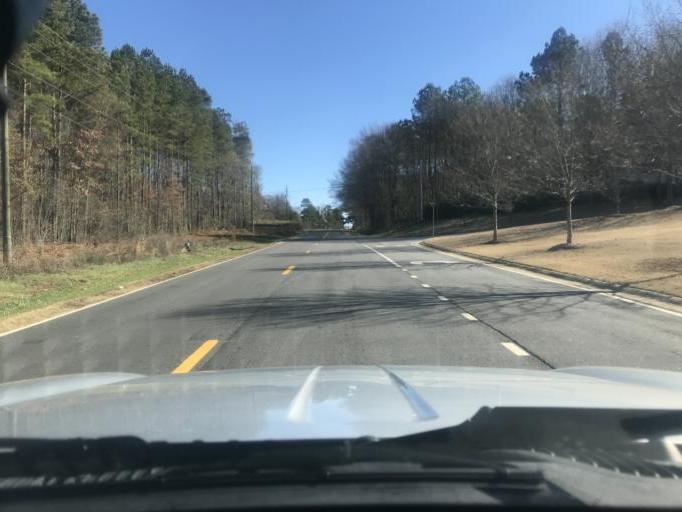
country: US
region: Georgia
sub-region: Barrow County
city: Russell
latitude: 33.9094
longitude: -83.7458
